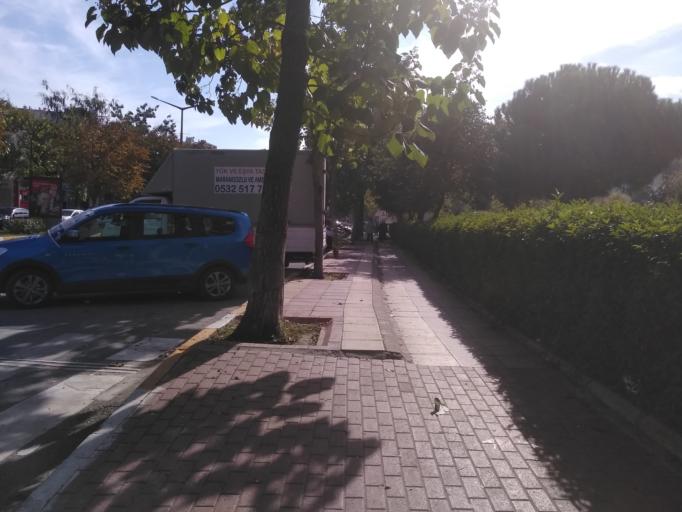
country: TR
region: Istanbul
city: Beylikduezue
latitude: 41.0075
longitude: 28.6433
